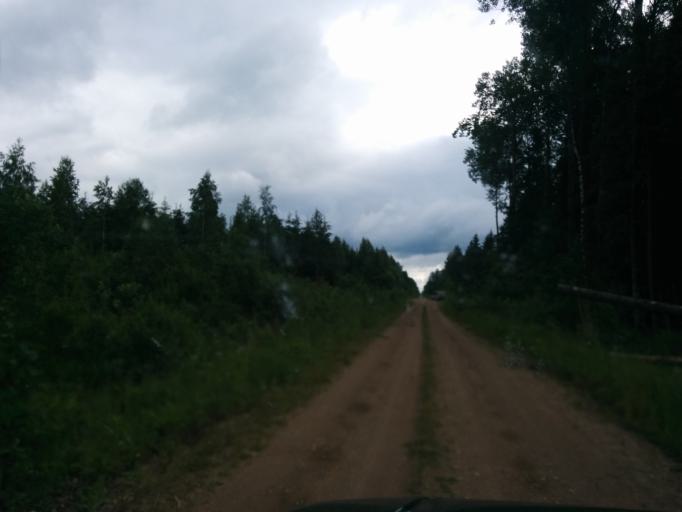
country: LV
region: Vilaka
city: Vilaka
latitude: 57.3924
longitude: 27.5808
